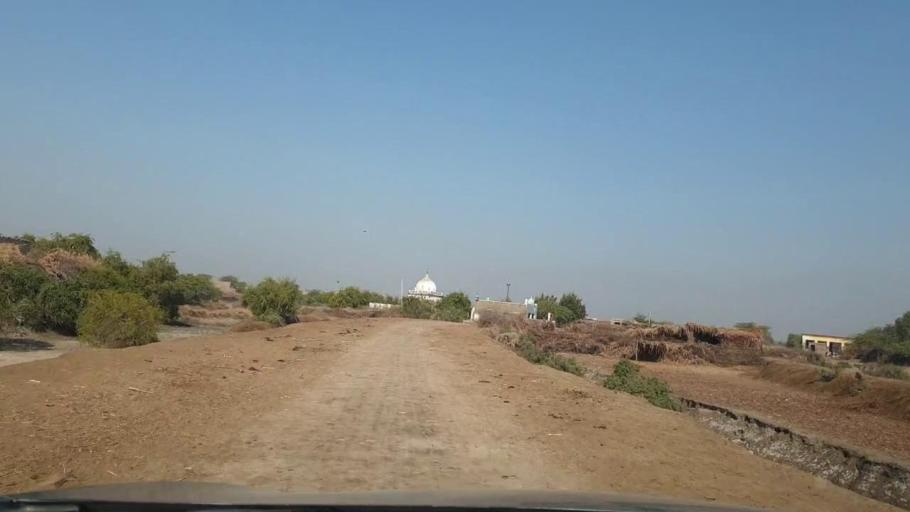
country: PK
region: Sindh
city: Mirpur Khas
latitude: 25.6280
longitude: 68.8912
